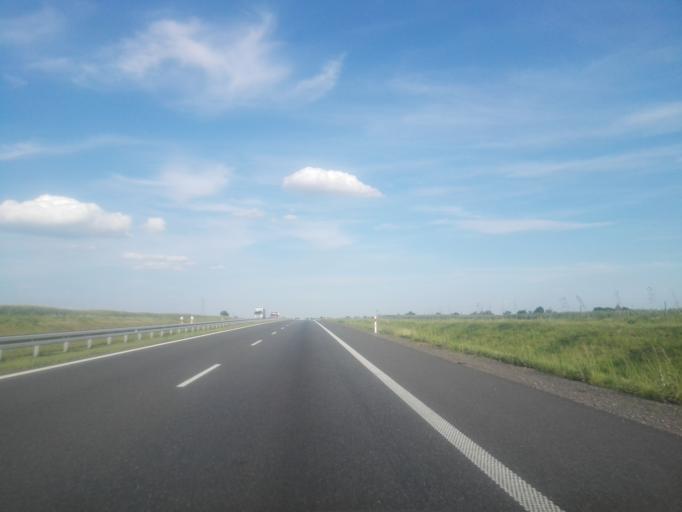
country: PL
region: Lower Silesian Voivodeship
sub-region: Powiat olesnicki
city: Sycow
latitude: 51.2987
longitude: 17.6557
